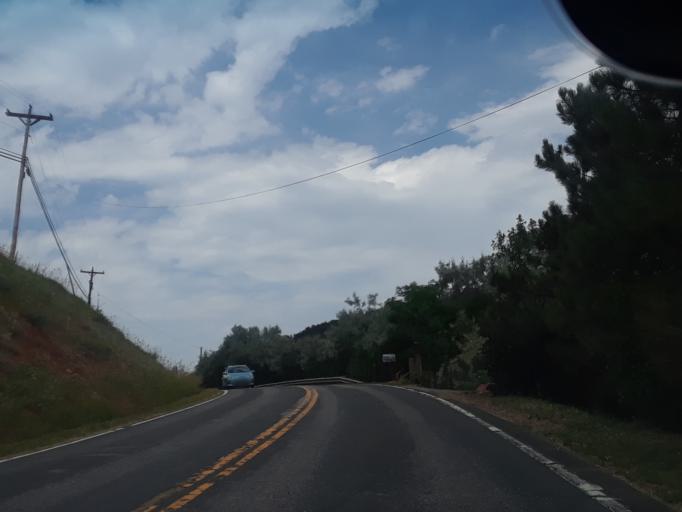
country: US
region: Colorado
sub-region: Boulder County
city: Boulder
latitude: 40.0822
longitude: -105.3024
